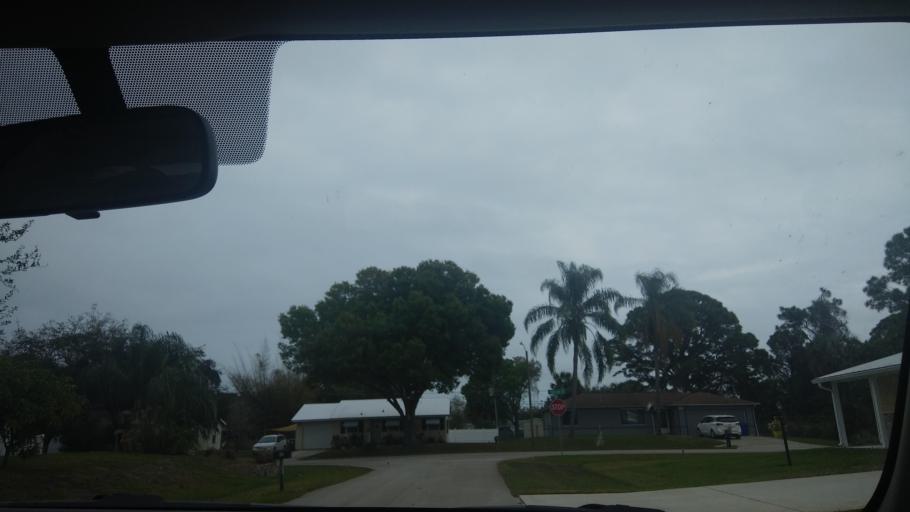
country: US
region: Florida
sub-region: Indian River County
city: Sebastian
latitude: 27.8008
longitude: -80.4879
